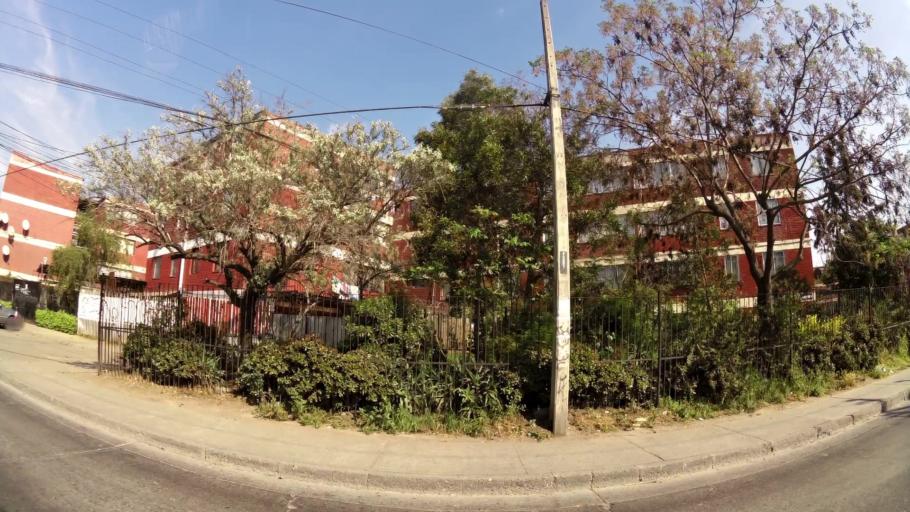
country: CL
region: Santiago Metropolitan
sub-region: Provincia de Santiago
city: La Pintana
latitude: -33.5606
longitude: -70.6620
